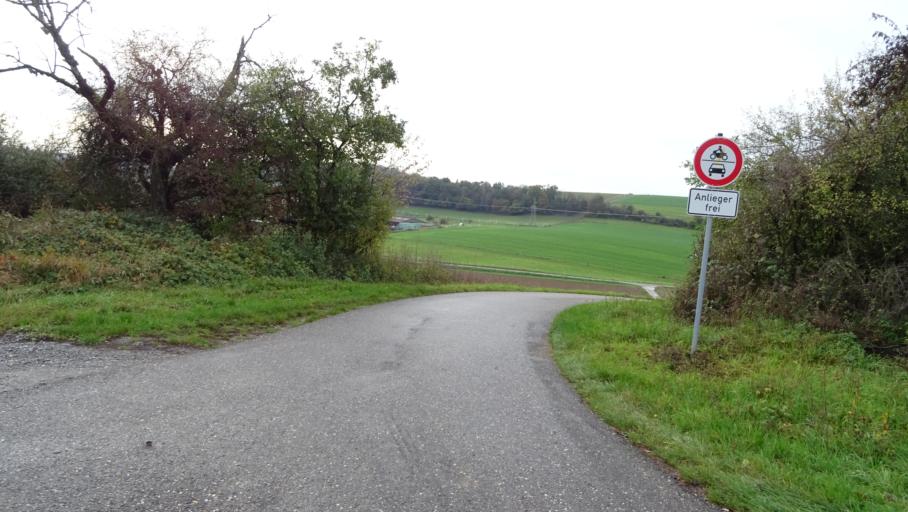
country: DE
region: Baden-Wuerttemberg
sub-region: Karlsruhe Region
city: Billigheim
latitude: 49.3483
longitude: 9.2071
